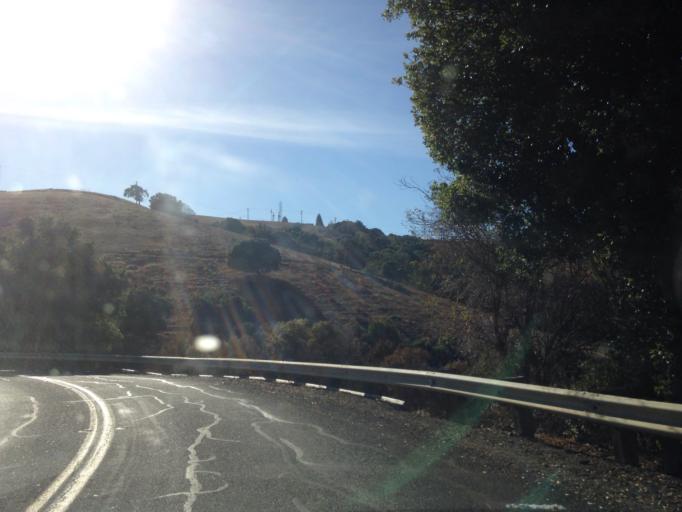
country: US
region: California
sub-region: Contra Costa County
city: Crockett
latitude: 38.0503
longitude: -122.1996
